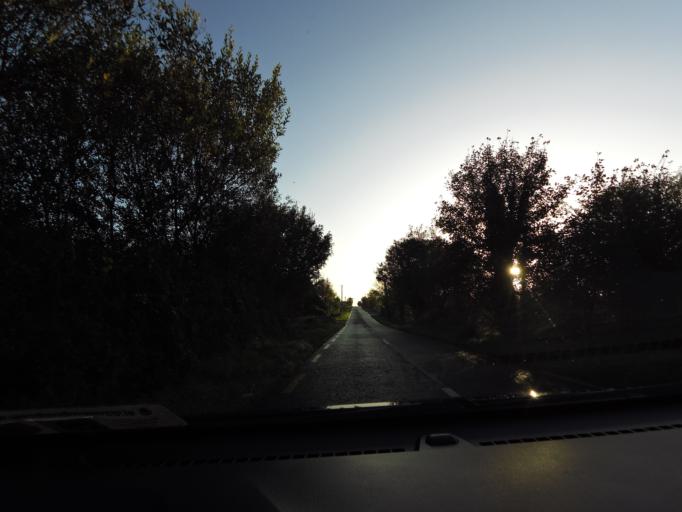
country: IE
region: Connaught
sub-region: Roscommon
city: Castlerea
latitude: 53.7480
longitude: -8.5343
